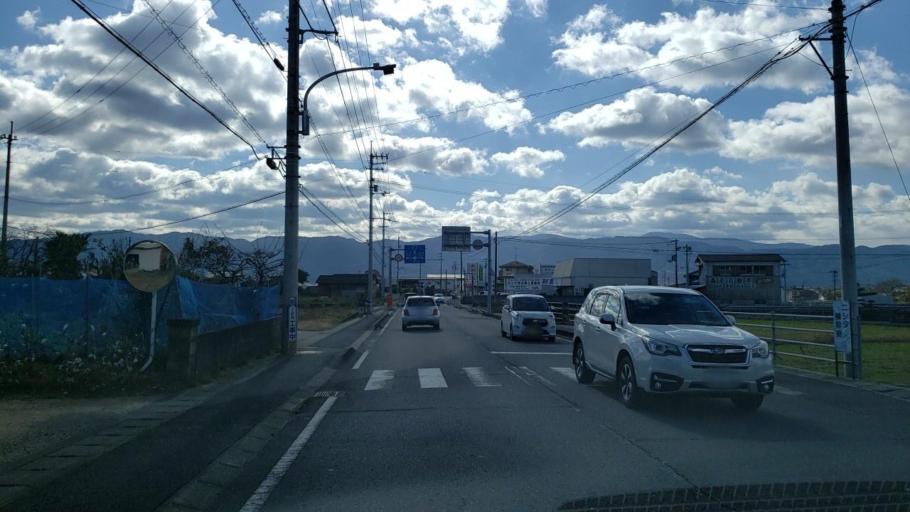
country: JP
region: Tokushima
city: Kamojimacho-jogejima
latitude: 34.1000
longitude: 134.3451
